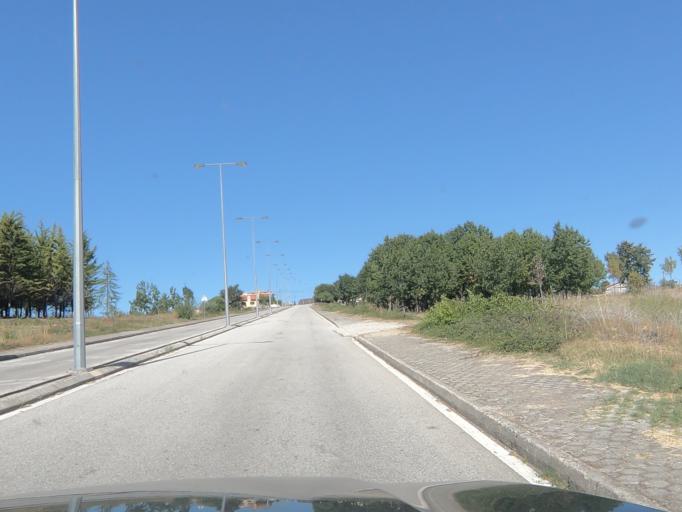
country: PT
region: Vila Real
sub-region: Valpacos
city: Valpacos
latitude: 41.6555
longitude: -7.3194
